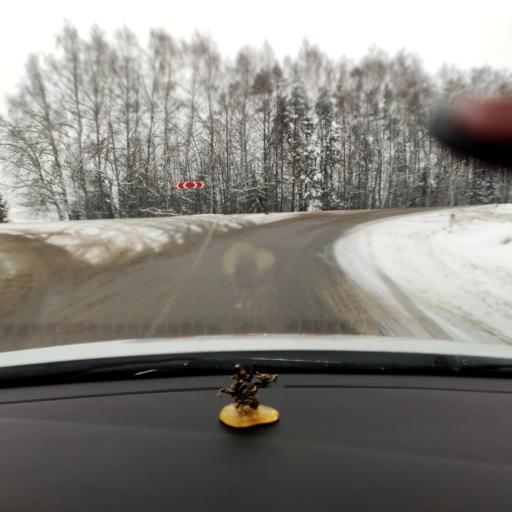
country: RU
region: Tatarstan
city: Vysokaya Gora
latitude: 56.1077
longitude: 49.1775
